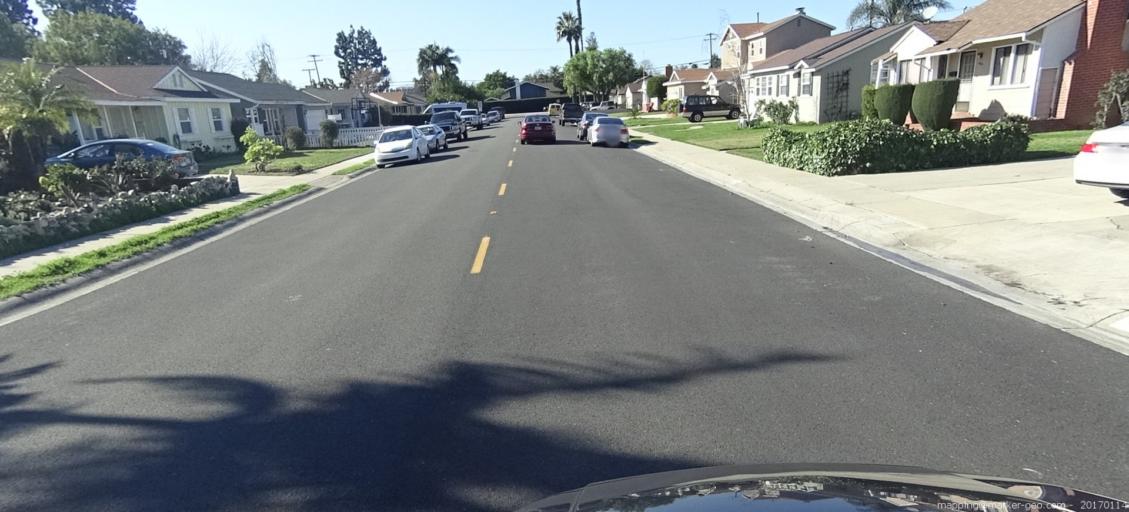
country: US
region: California
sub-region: Orange County
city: Tustin
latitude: 33.7543
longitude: -117.8207
